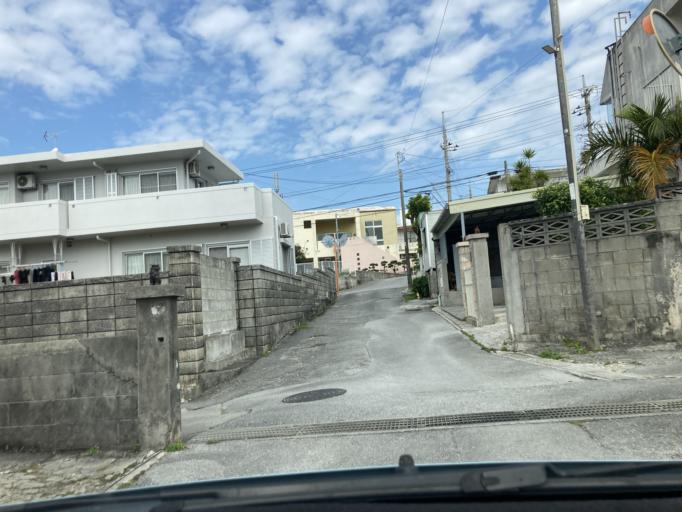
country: JP
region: Okinawa
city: Tomigusuku
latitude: 26.1865
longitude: 127.6924
